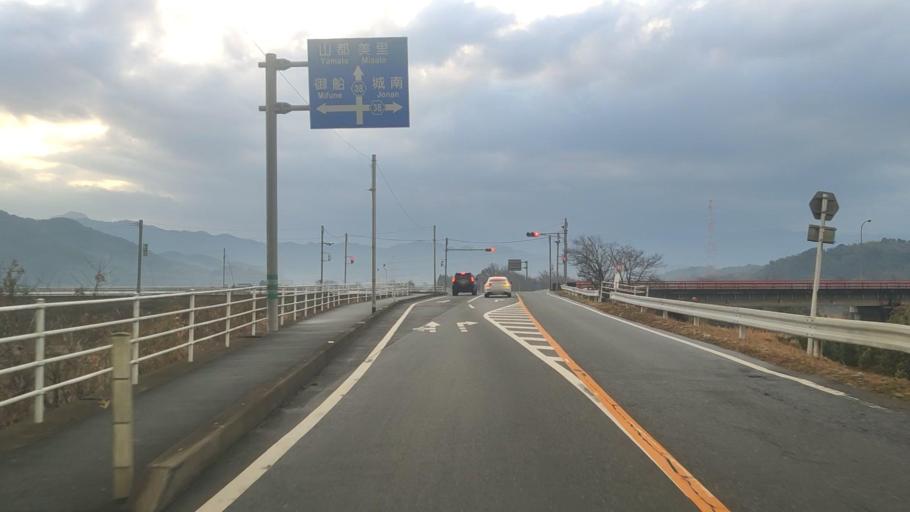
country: JP
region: Kumamoto
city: Uto
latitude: 32.6936
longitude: 130.7902
